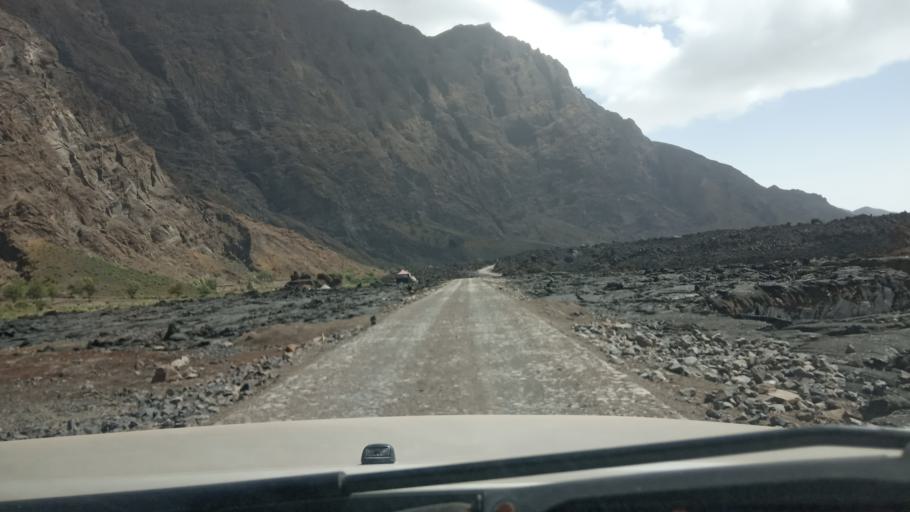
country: CV
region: Mosteiros
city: Porto dos Mosteiros
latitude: 14.9491
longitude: -24.3854
